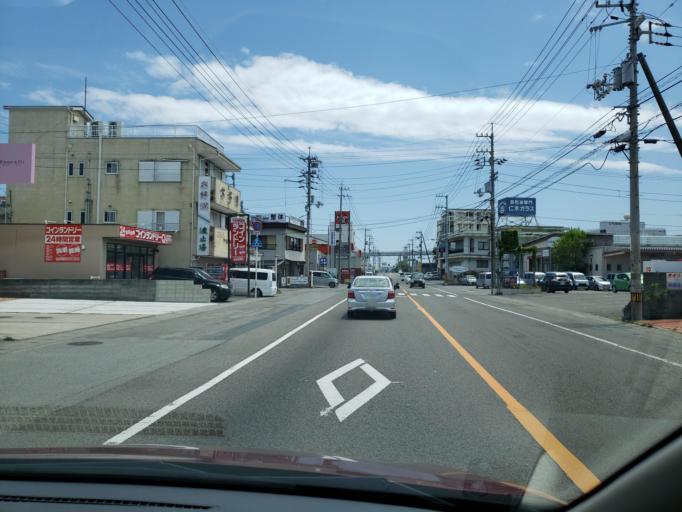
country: JP
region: Tokushima
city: Tokushima-shi
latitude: 34.0593
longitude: 134.5825
